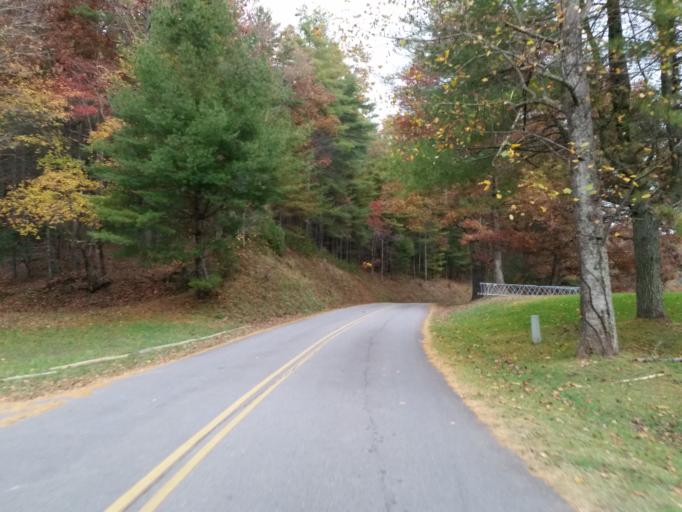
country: US
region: Georgia
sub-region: Fannin County
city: Blue Ridge
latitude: 34.7641
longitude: -84.1787
